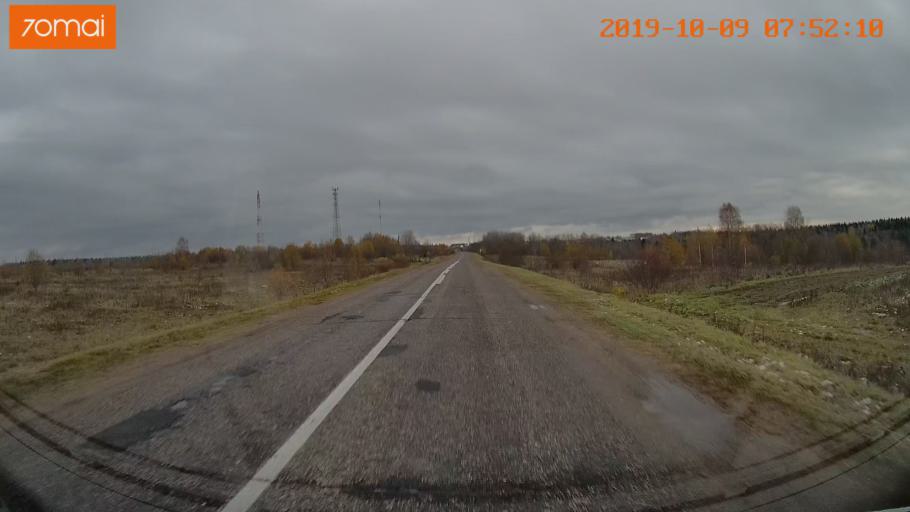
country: RU
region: Jaroslavl
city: Kukoboy
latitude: 58.6889
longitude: 39.8831
